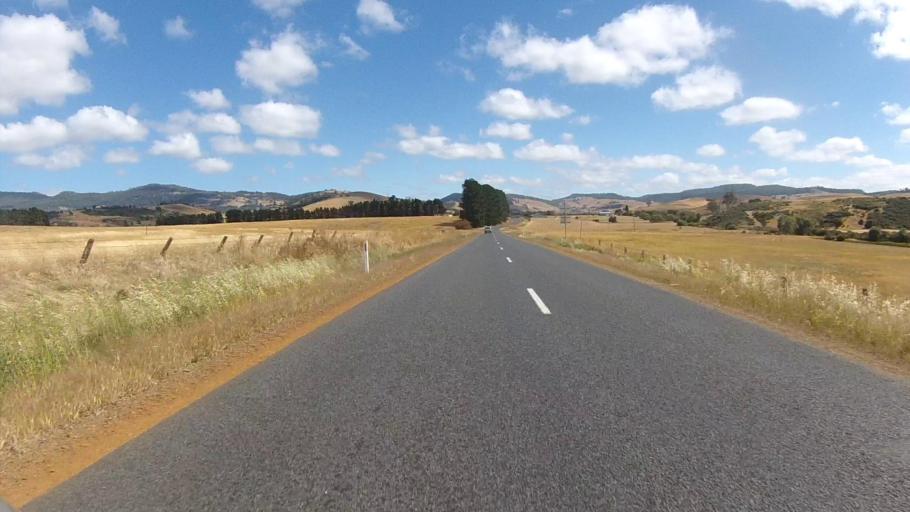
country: AU
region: Tasmania
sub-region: Brighton
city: Bridgewater
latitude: -42.5522
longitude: 147.3803
